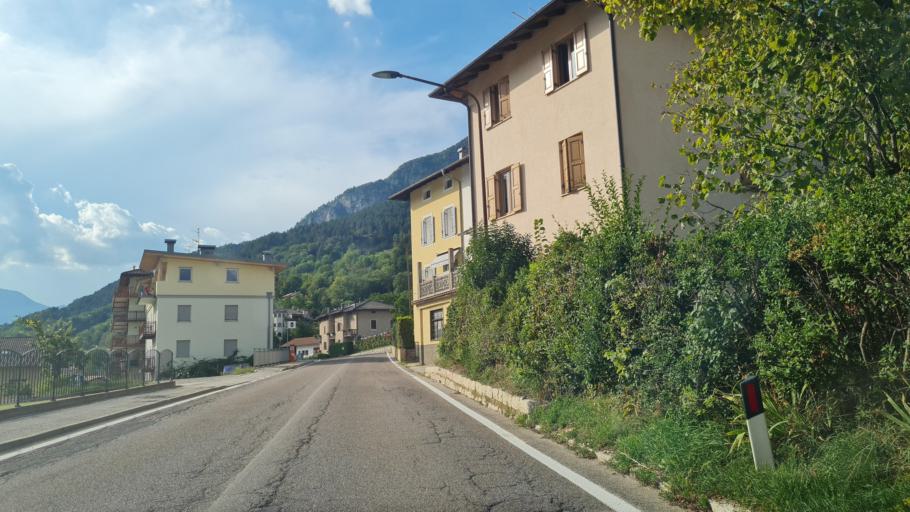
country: IT
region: Trentino-Alto Adige
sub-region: Provincia di Trento
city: Vigolo Vattaro
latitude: 46.0050
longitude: 11.1945
